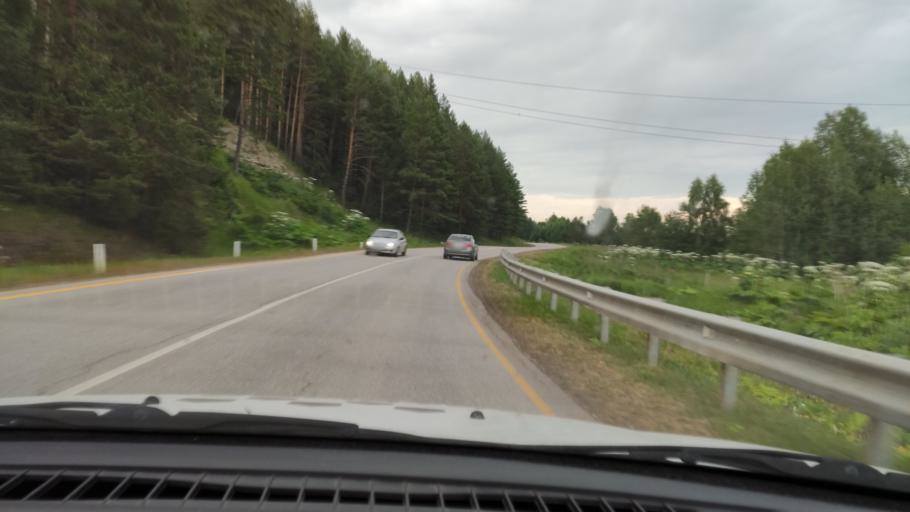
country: RU
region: Perm
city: Kukushtan
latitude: 57.4892
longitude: 56.6299
